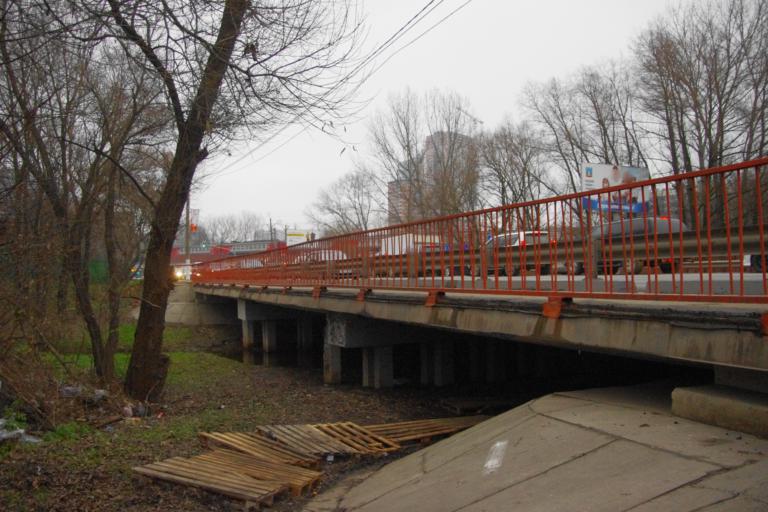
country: RU
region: Moskovskaya
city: Pavshino
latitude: 55.8182
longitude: 37.3505
